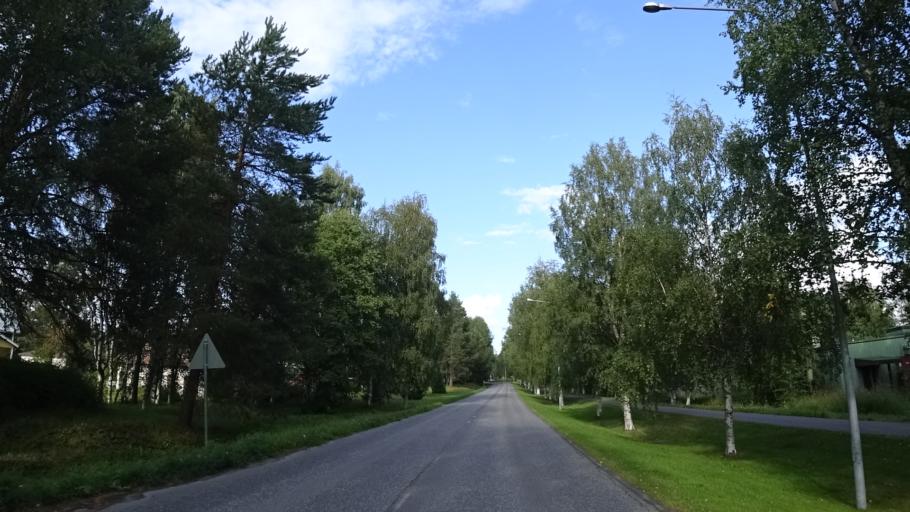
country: FI
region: North Karelia
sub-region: Pielisen Karjala
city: Lieksa
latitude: 63.3300
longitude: 30.0256
